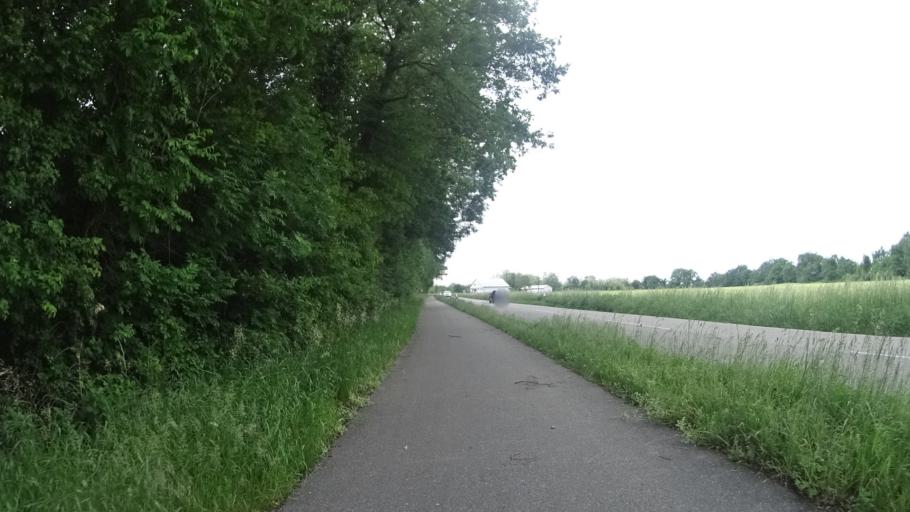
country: DE
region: Baden-Wuerttemberg
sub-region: Freiburg Region
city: Neuenburg am Rhein
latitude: 47.7854
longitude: 7.5555
